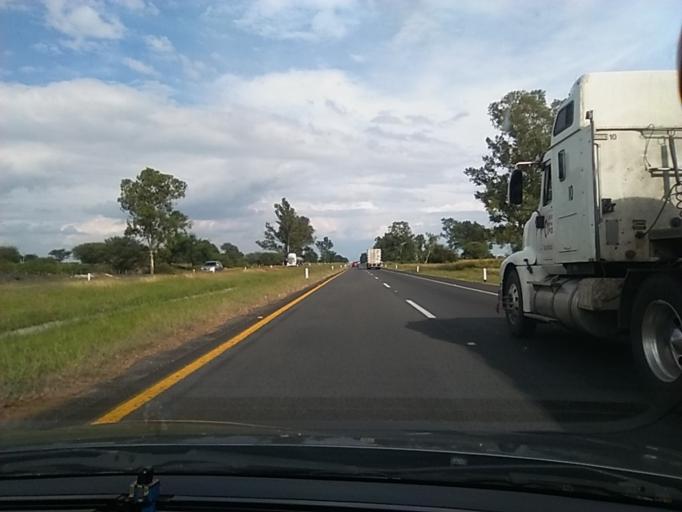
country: MX
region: Jalisco
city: La Barca
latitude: 20.3222
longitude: -102.5562
